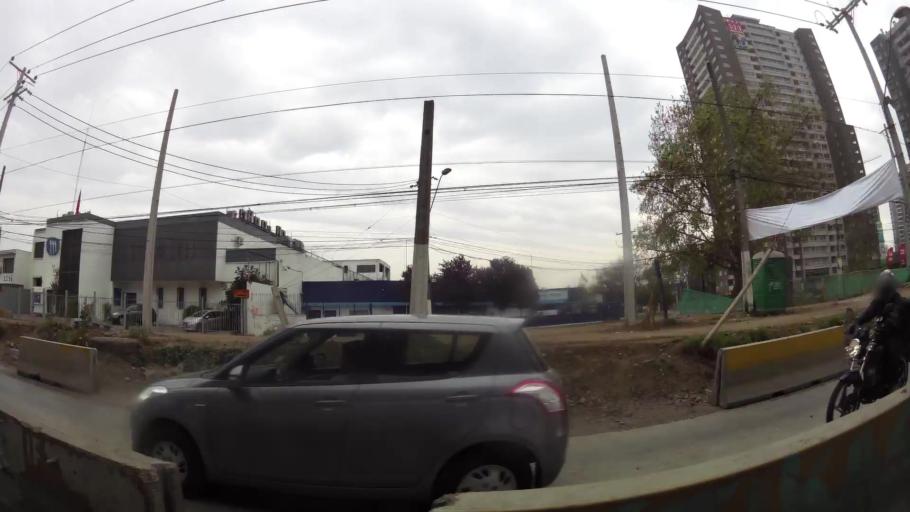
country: CL
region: Santiago Metropolitan
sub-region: Provincia de Santiago
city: Santiago
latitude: -33.4723
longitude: -70.6238
